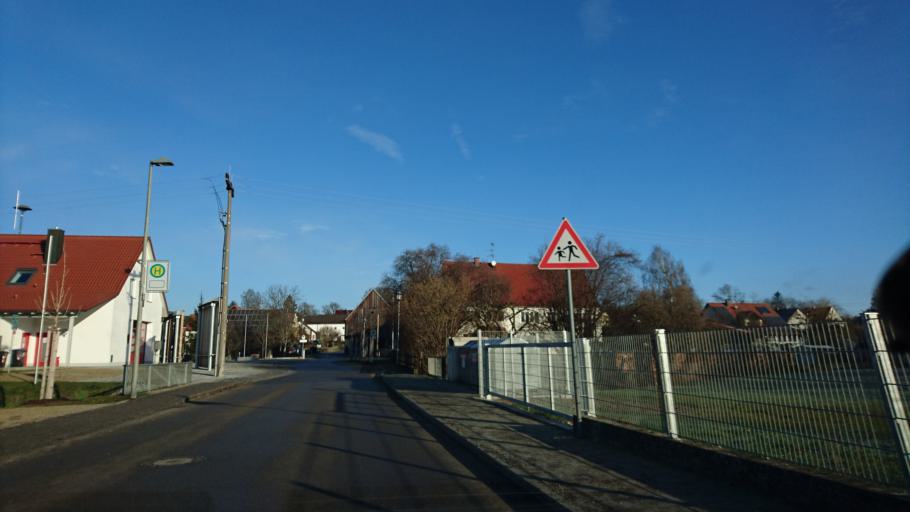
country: DE
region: Bavaria
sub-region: Swabia
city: Kuhlenthal
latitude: 48.5521
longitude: 10.7900
